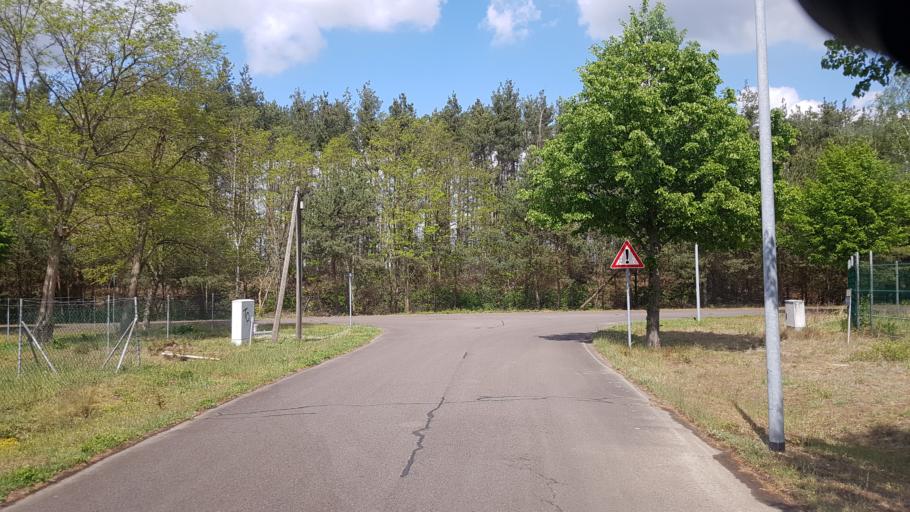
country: DE
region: Brandenburg
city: Altdobern
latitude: 51.6478
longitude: 14.0002
